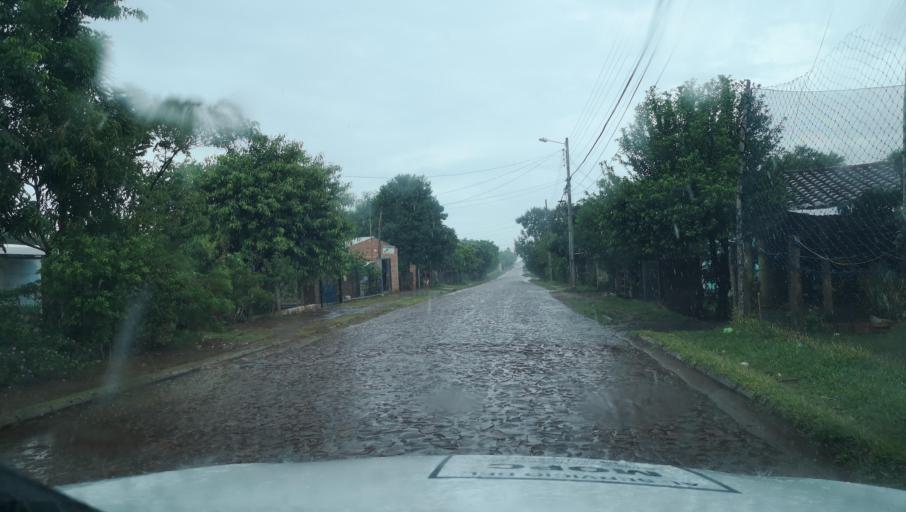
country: PY
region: Misiones
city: Santa Maria
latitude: -26.8971
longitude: -57.0333
